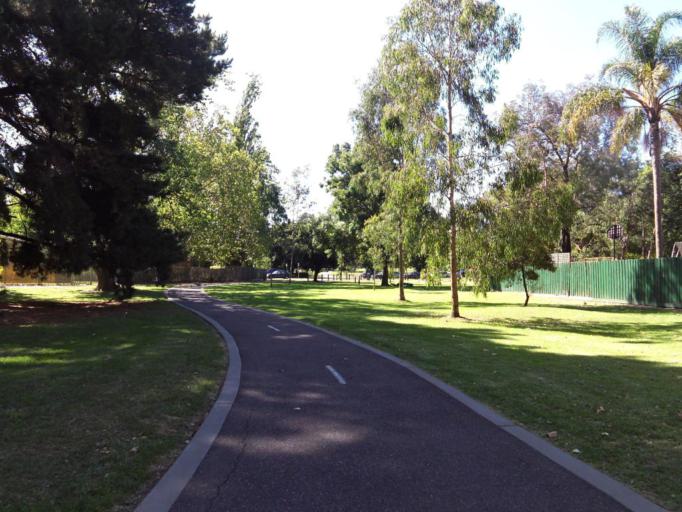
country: AU
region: Victoria
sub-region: Boroondara
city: Kew East
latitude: -37.7945
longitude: 145.0611
